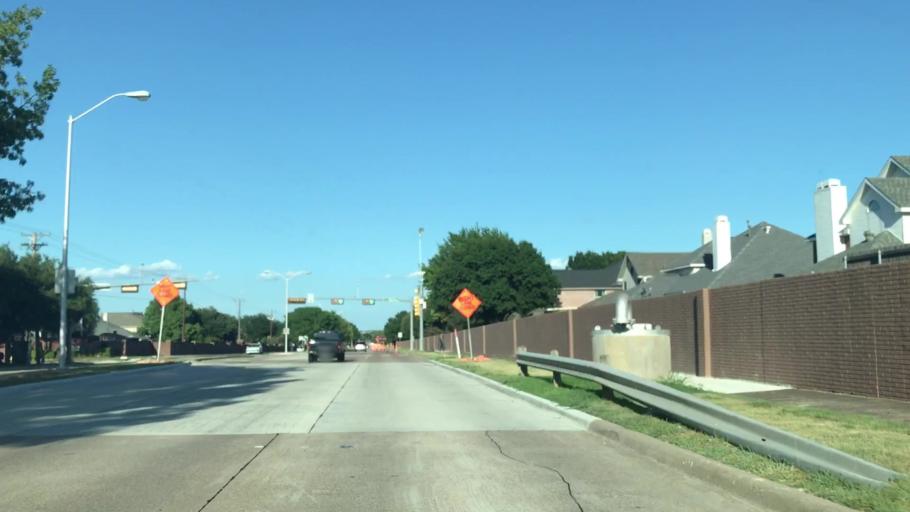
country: US
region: Texas
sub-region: Collin County
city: Plano
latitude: 33.0714
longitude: -96.7259
